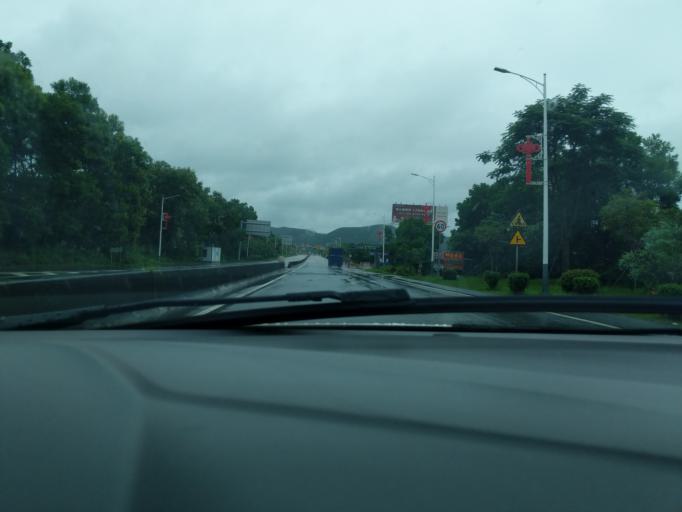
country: CN
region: Guangdong
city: Pingshi
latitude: 22.2345
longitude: 112.3094
